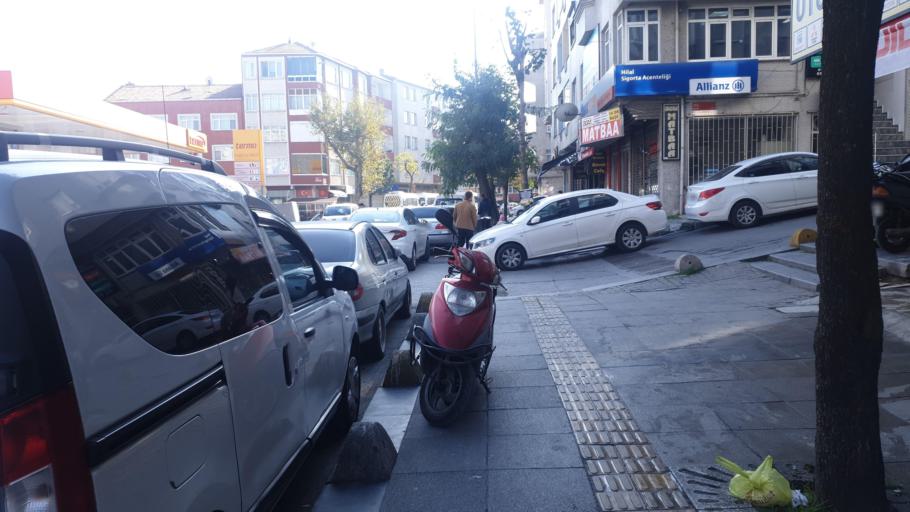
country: TR
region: Istanbul
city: Esenler
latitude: 41.0698
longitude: 28.9028
